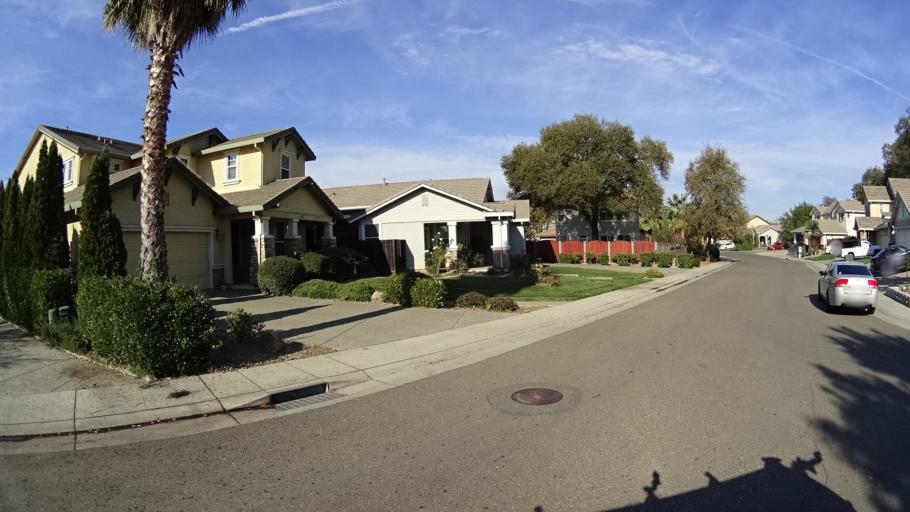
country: US
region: California
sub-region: Sacramento County
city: Citrus Heights
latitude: 38.6845
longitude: -121.2950
